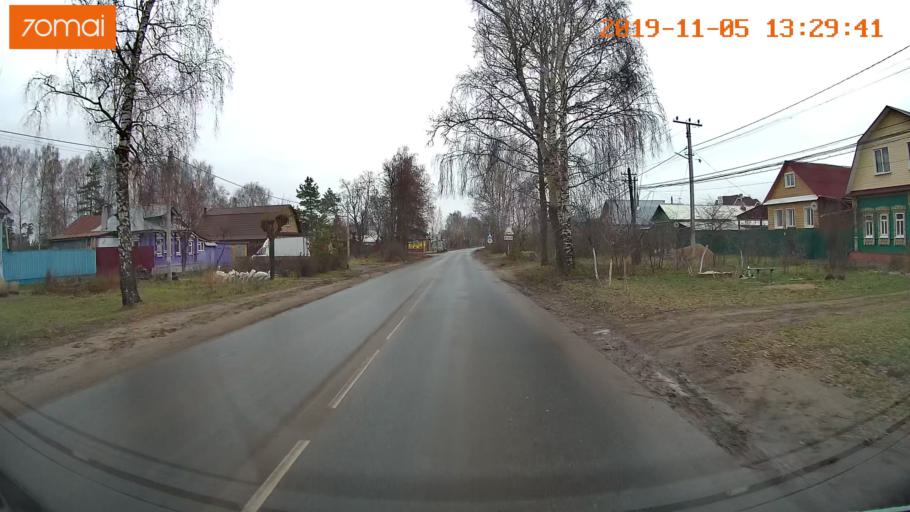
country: RU
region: Ivanovo
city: Shuya
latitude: 56.8624
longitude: 41.3973
